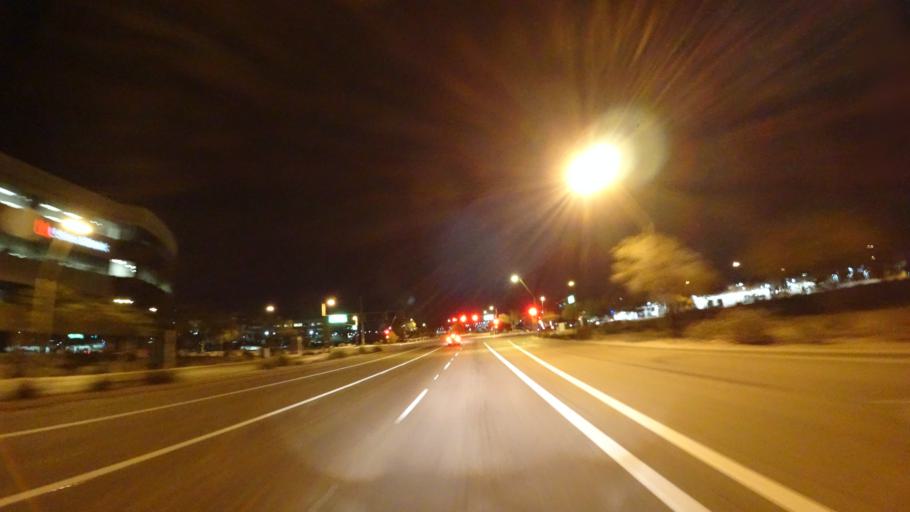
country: US
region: Arizona
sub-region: Maricopa County
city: Tempe Junction
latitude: 33.4421
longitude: -111.9574
